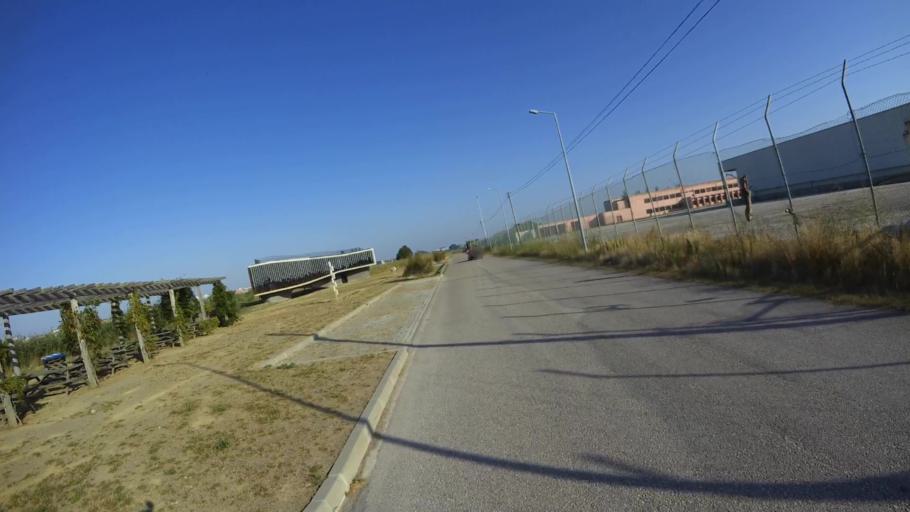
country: PT
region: Aveiro
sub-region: Aveiro
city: Aveiro
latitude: 40.6396
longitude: -8.6717
